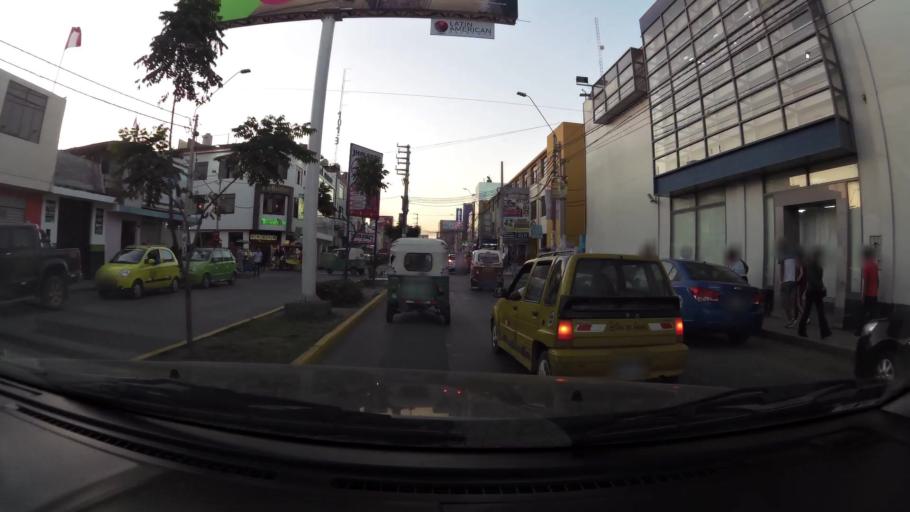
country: PE
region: Ica
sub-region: Provincia de Ica
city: Ica
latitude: -14.0662
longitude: -75.7301
